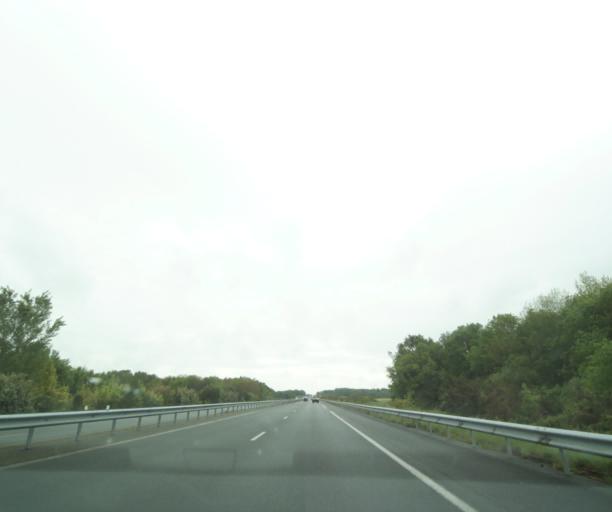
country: FR
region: Poitou-Charentes
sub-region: Departement de la Charente-Maritime
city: Chermignac
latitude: 45.7008
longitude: -0.7285
